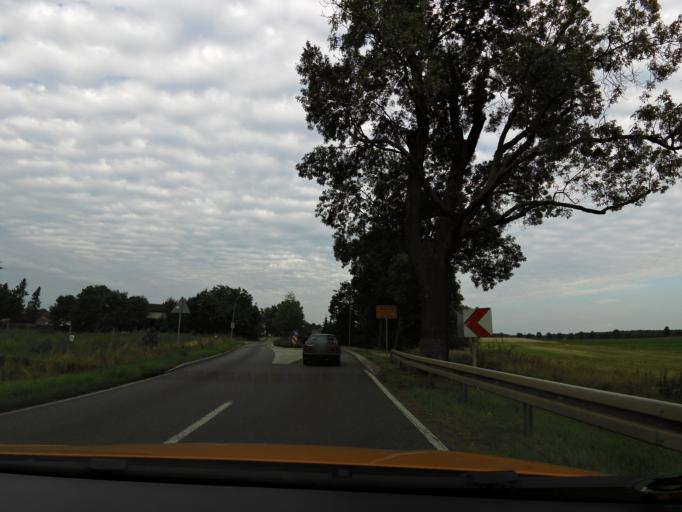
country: DE
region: Brandenburg
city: Roskow
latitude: 52.4087
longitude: 12.6874
